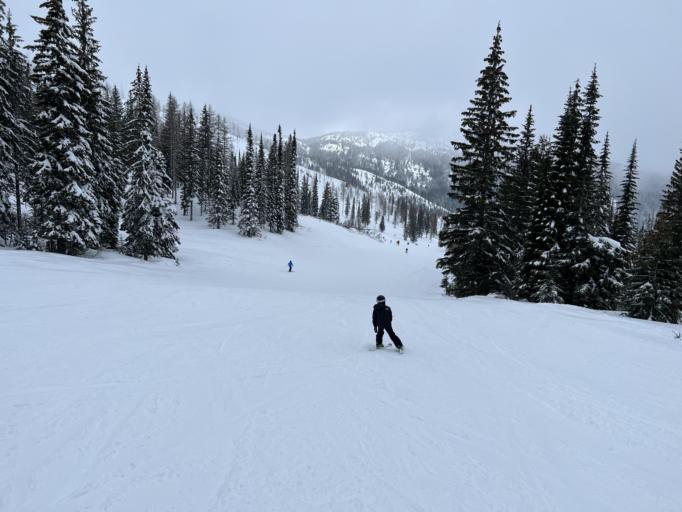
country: US
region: Idaho
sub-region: Bonner County
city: Ponderay
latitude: 48.3818
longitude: -116.6186
